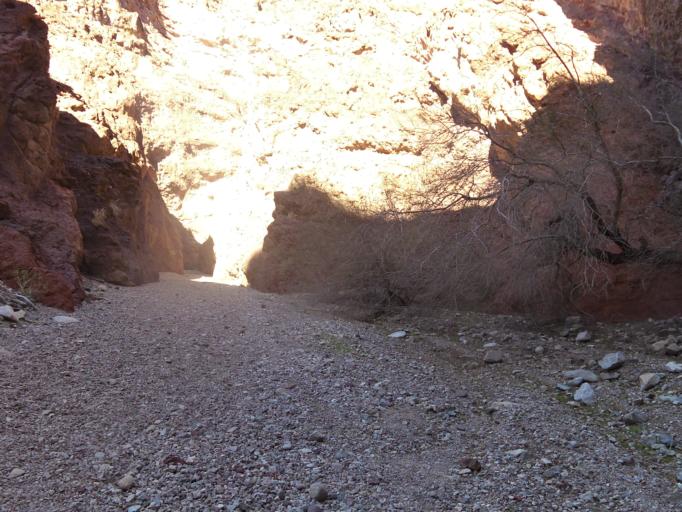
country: US
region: Nevada
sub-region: Clark County
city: Boulder City
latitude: 35.9642
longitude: -114.7269
